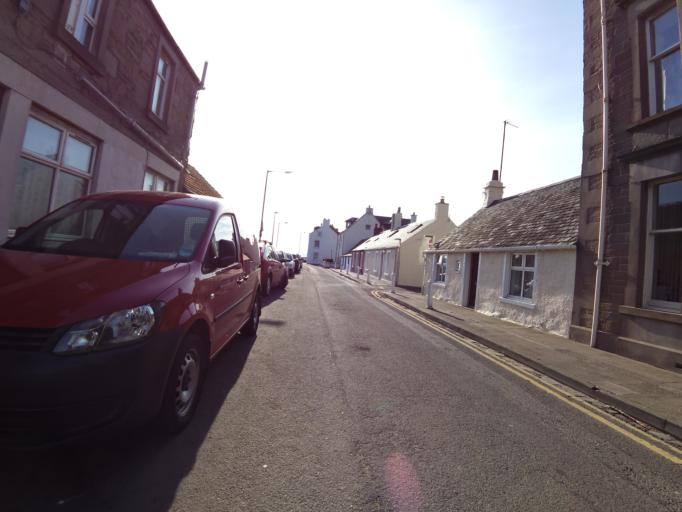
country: GB
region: Scotland
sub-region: Fife
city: Tayport
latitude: 56.4648
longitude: -2.8734
